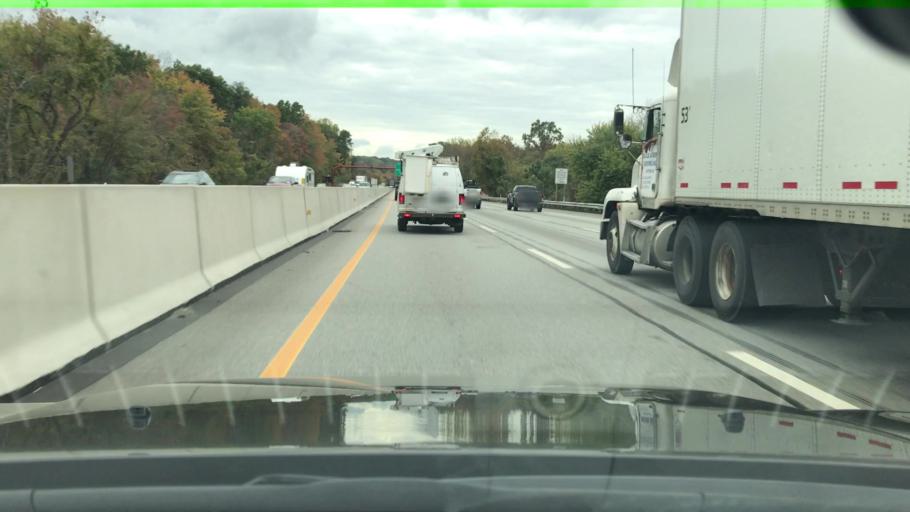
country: US
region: Pennsylvania
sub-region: Montgomery County
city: Dresher
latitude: 40.1497
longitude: -75.1482
